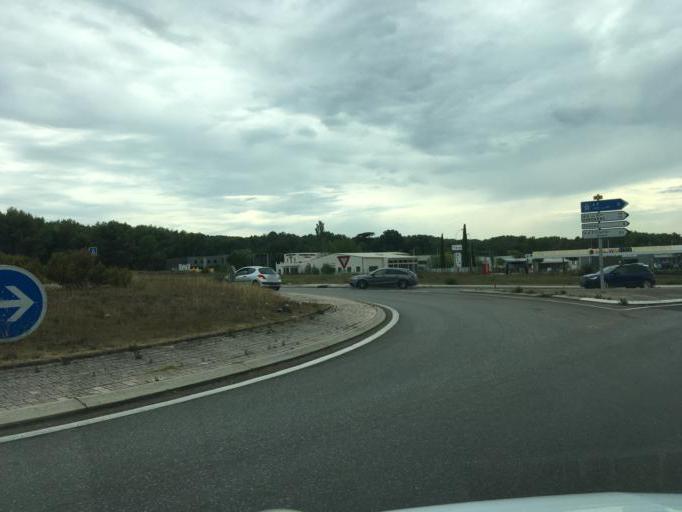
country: FR
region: Provence-Alpes-Cote d'Azur
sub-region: Departement des Bouches-du-Rhone
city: Rousset
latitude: 43.4638
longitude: 5.6111
